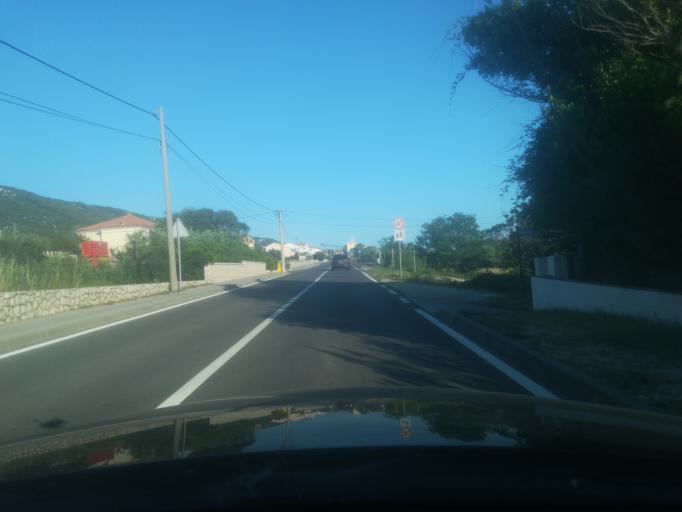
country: HR
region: Primorsko-Goranska
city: Banjol
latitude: 44.7728
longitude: 14.7601
